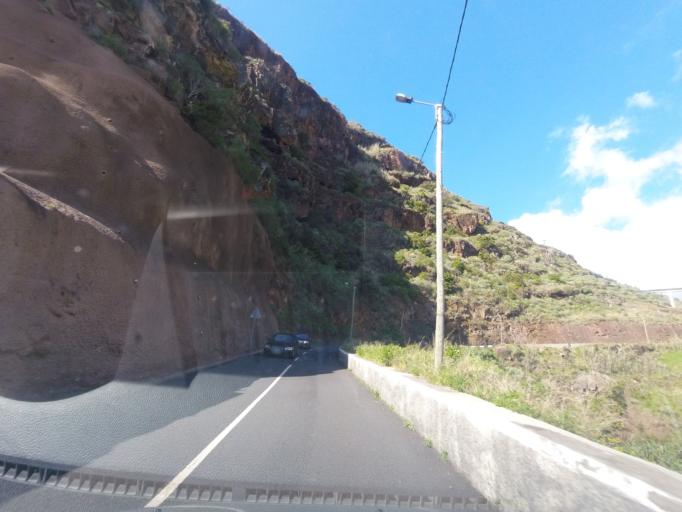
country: PT
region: Madeira
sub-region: Calheta
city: Estreito da Calheta
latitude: 32.7358
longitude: -17.2005
